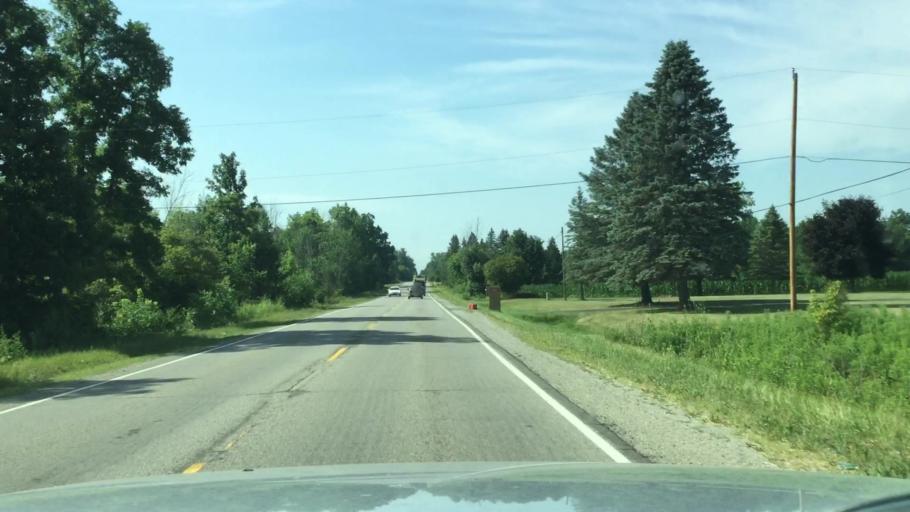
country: US
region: Michigan
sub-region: Genesee County
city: Flushing
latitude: 43.1280
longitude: -83.8138
